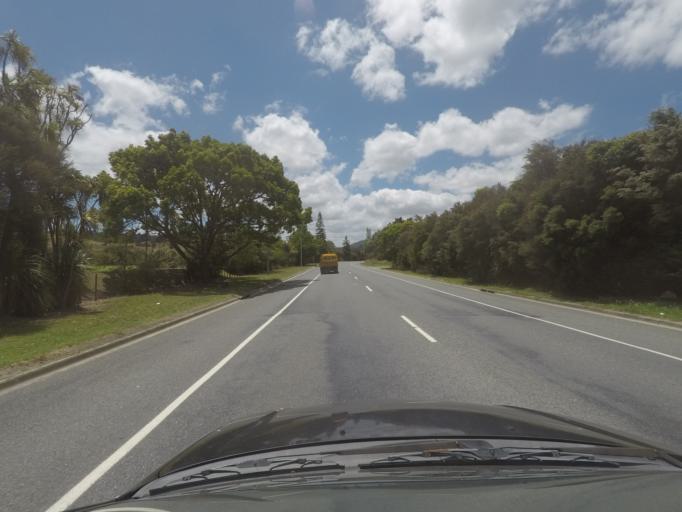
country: NZ
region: Northland
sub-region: Whangarei
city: Whangarei
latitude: -35.7485
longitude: 174.3206
